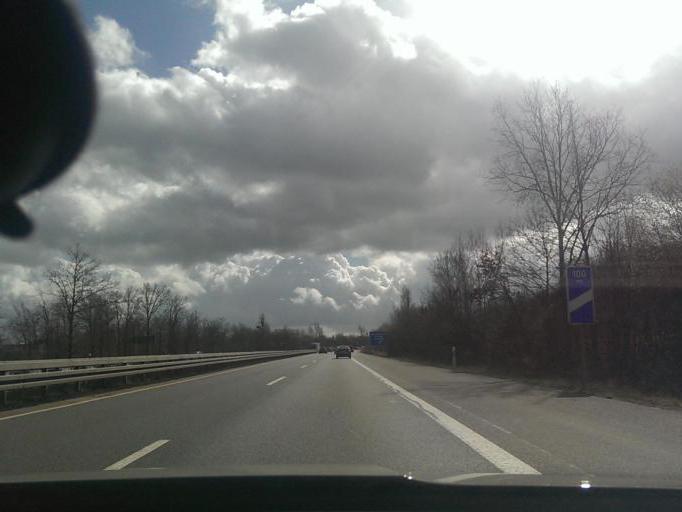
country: DE
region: Lower Saxony
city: Wolfsburg
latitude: 52.4153
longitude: 10.7363
